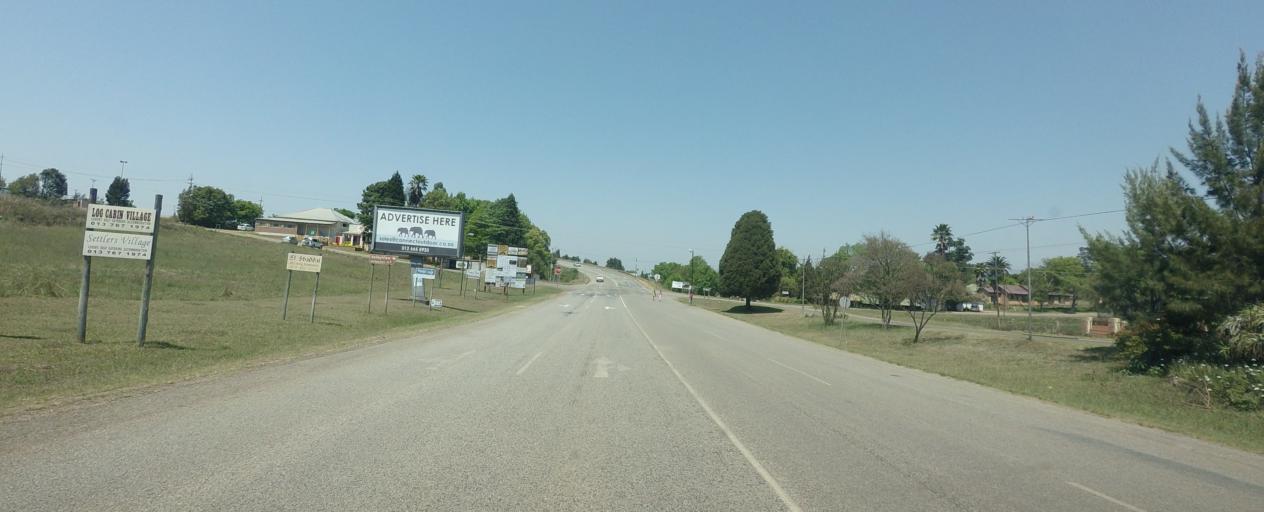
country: ZA
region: Mpumalanga
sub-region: Ehlanzeni District
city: Graksop
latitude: -24.9309
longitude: 30.8377
